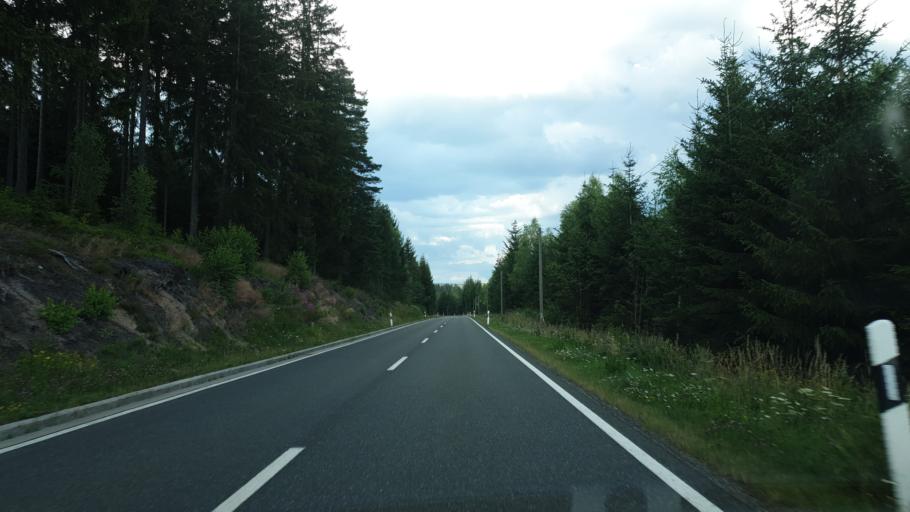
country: DE
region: Saxony
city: Tannenbergsthal
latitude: 50.4522
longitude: 12.4577
